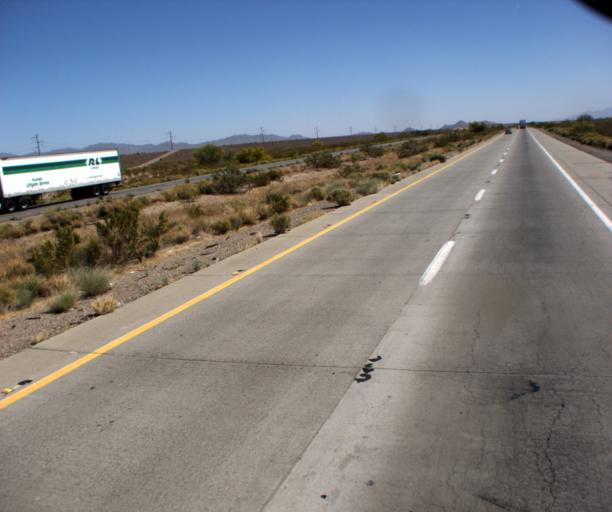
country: US
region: Arizona
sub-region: Maricopa County
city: Buckeye
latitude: 33.4510
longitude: -112.7306
